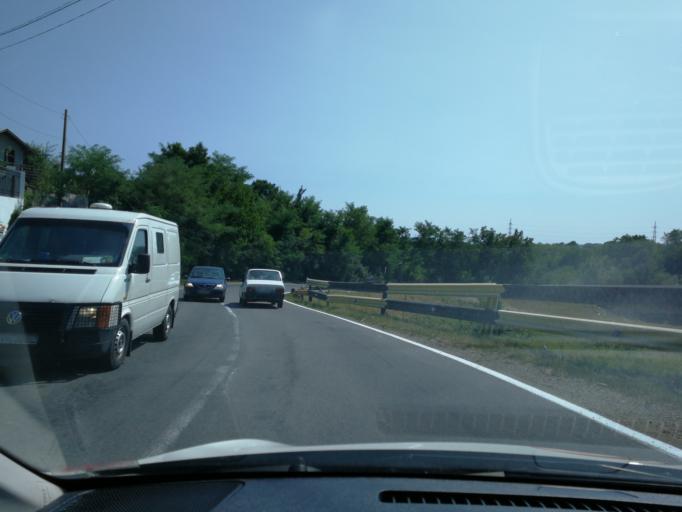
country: RO
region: Prahova
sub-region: Comuna Izvoarele
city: Homoraciu
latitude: 45.2507
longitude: 26.0247
